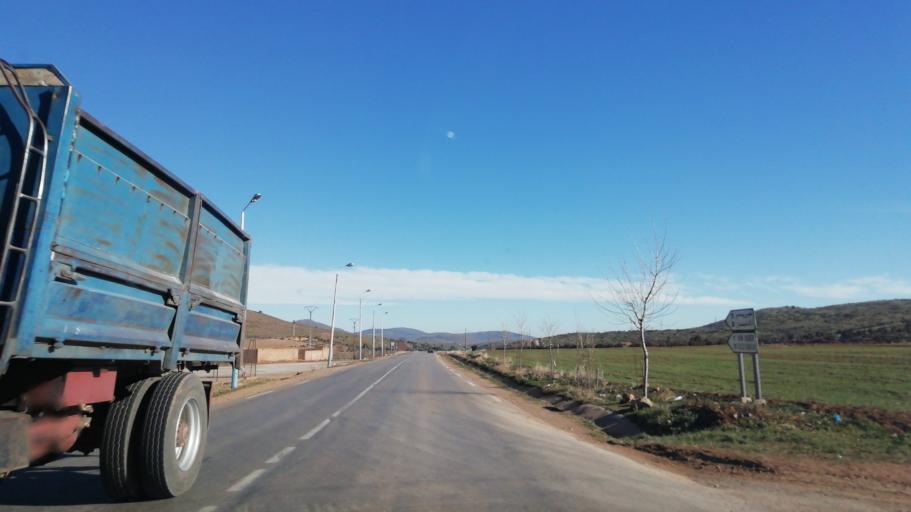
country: DZ
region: Tlemcen
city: Sebdou
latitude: 34.7435
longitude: -1.1663
